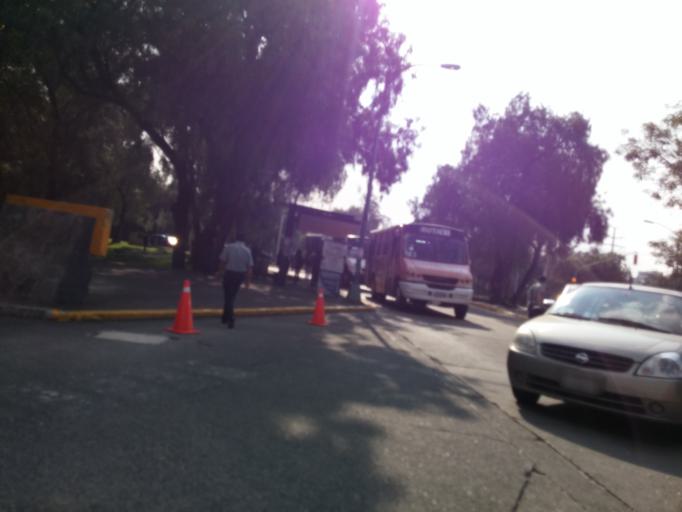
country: MX
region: Mexico City
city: Magdalena Contreras
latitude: 19.3345
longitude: -99.1890
